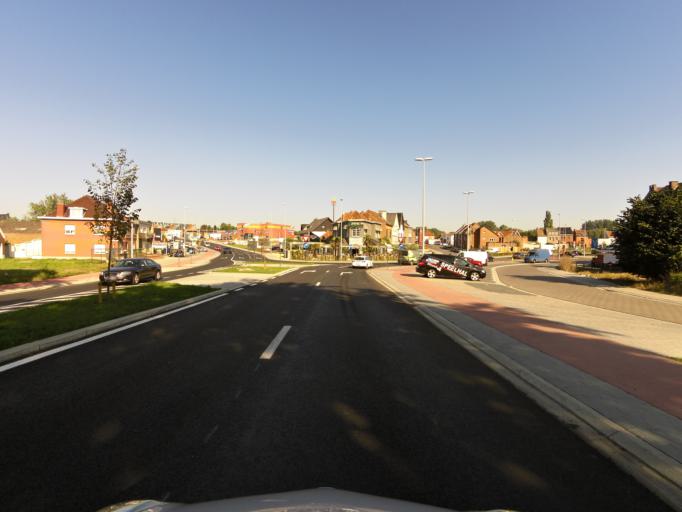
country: BE
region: Flanders
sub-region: Provincie Oost-Vlaanderen
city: Ninove
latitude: 50.8356
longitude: 4.0091
